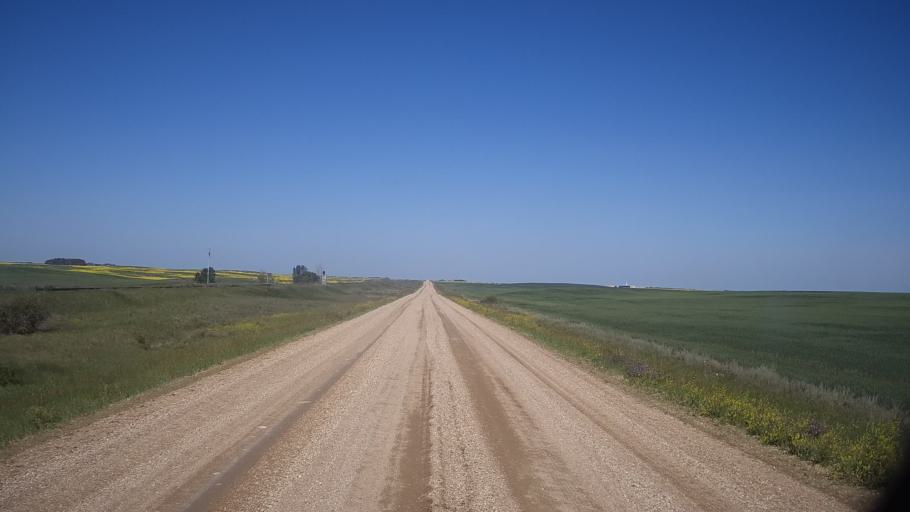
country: CA
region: Saskatchewan
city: Watrous
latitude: 51.8486
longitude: -105.9290
